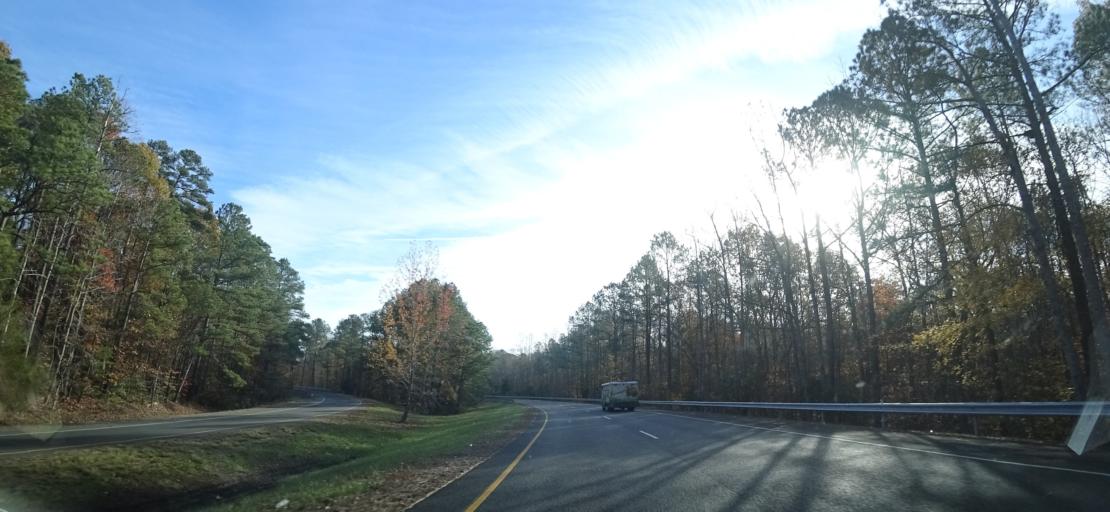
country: US
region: Virginia
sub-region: New Kent County
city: New Kent
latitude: 37.4772
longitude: -76.9220
